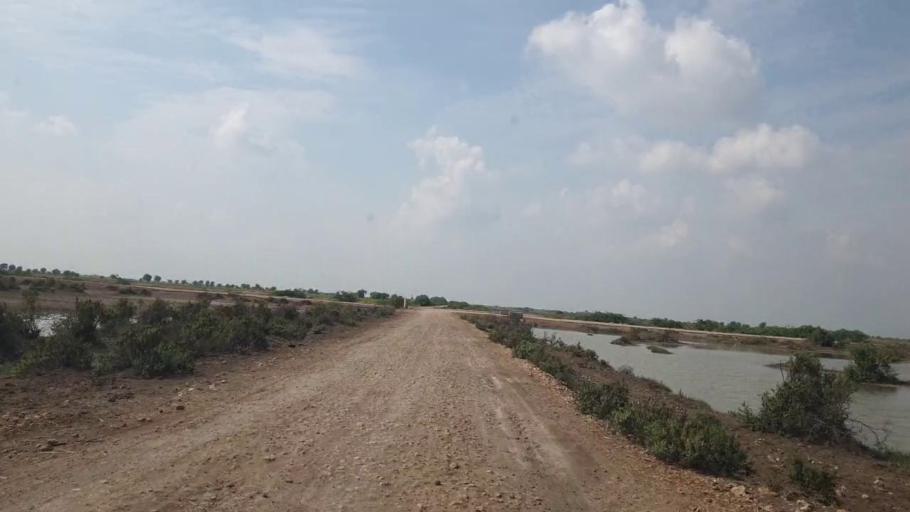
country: PK
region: Sindh
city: Badin
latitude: 24.5066
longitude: 68.6092
